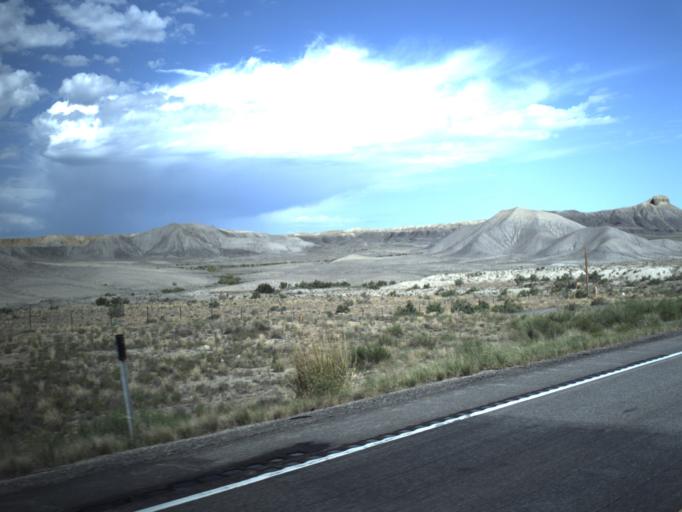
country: US
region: Utah
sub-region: Carbon County
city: East Carbon City
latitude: 39.3301
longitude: -110.3683
